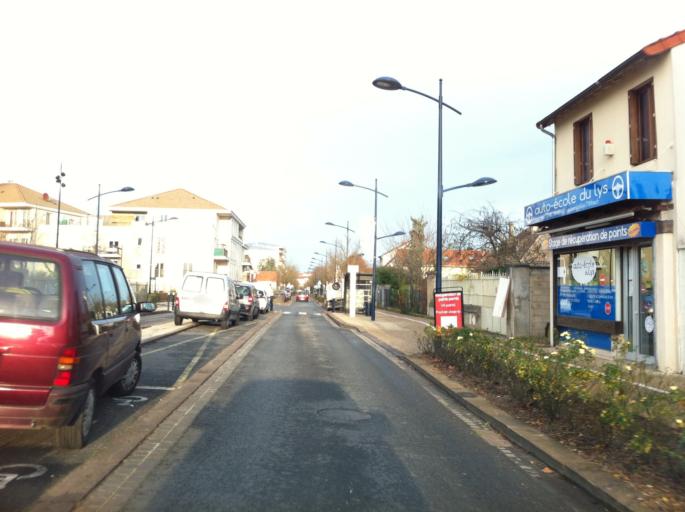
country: FR
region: Ile-de-France
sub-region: Departement de Seine-et-Marne
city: Dammarie-les-Lys
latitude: 48.5195
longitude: 2.6405
